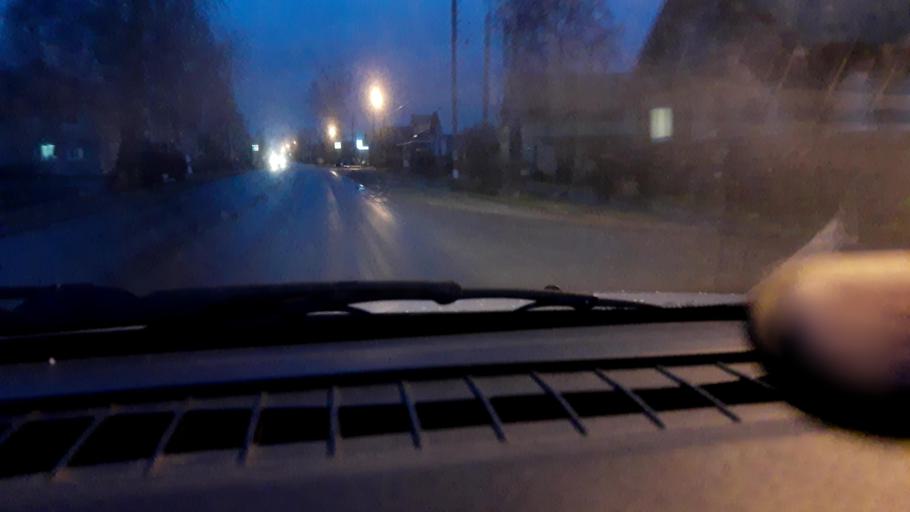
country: RU
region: Nizjnij Novgorod
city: Uren'
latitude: 57.4533
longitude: 45.7789
